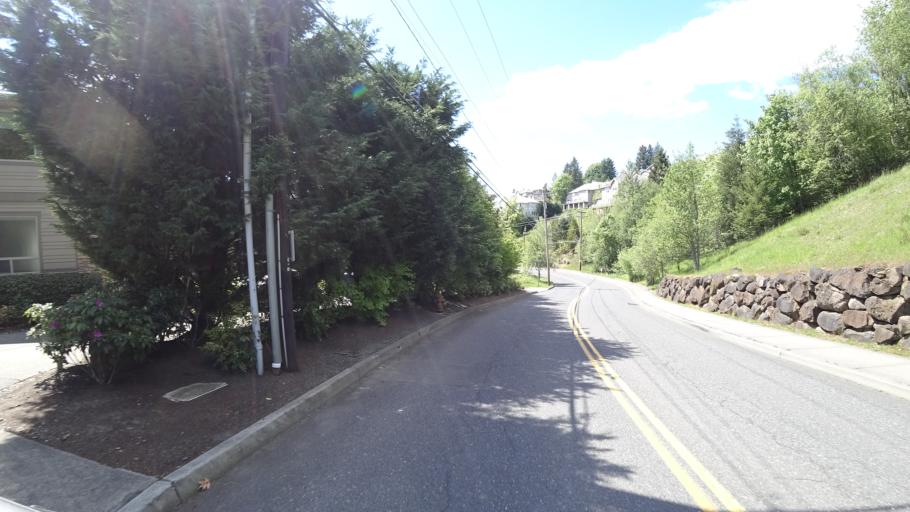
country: US
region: Oregon
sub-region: Washington County
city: West Haven
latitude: 45.5487
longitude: -122.7755
